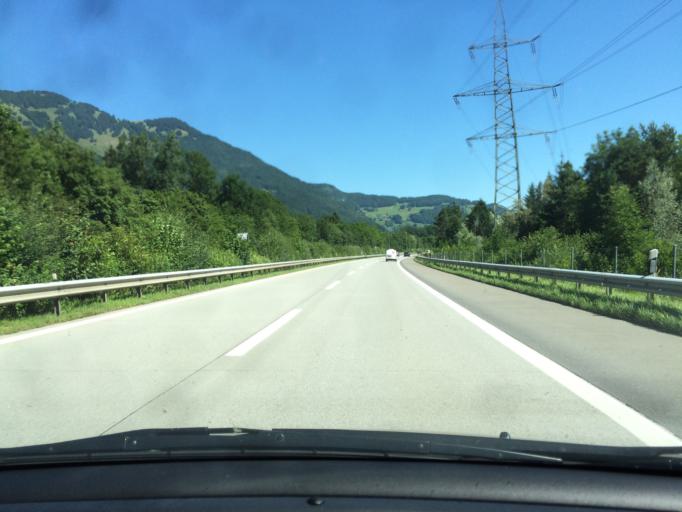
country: CH
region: Saint Gallen
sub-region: Wahlkreis Werdenberg
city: Sennwald
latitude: 47.2681
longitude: 9.5285
